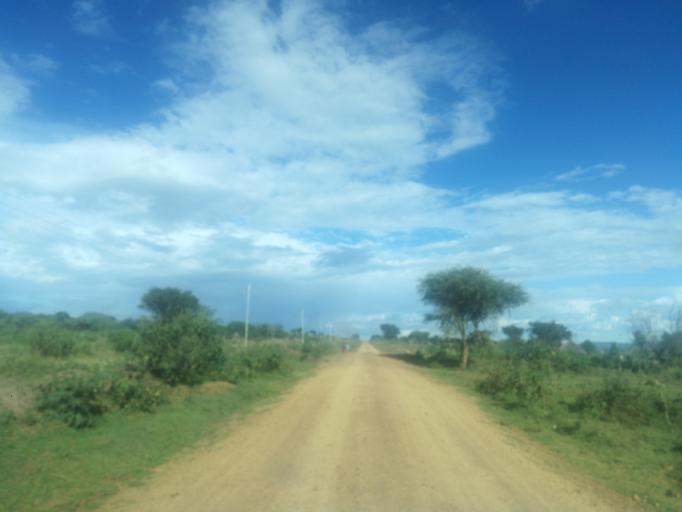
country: TZ
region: Mara
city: Issenye
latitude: -1.7545
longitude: 34.2554
